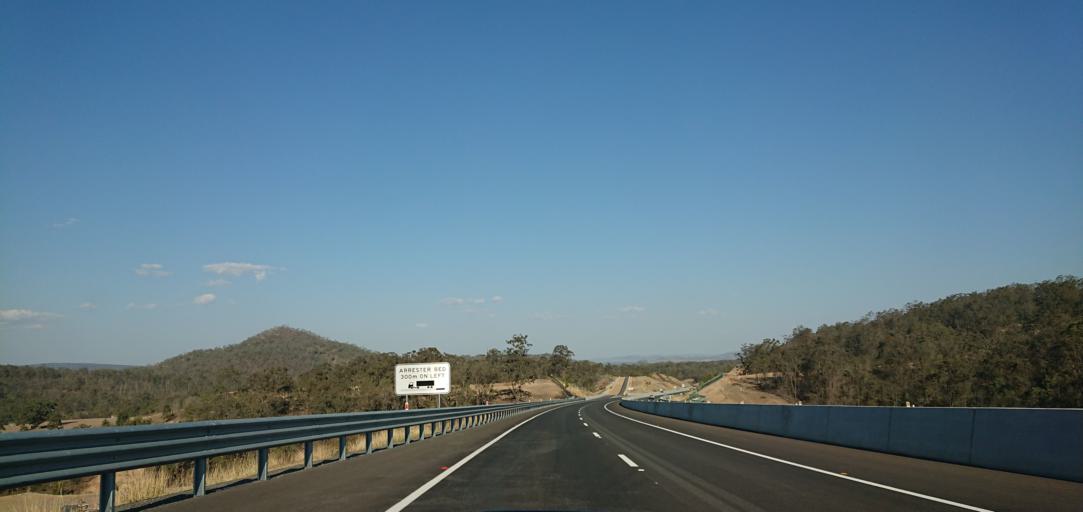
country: AU
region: Queensland
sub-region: Toowoomba
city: East Toowoomba
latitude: -27.5082
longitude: 152.0120
